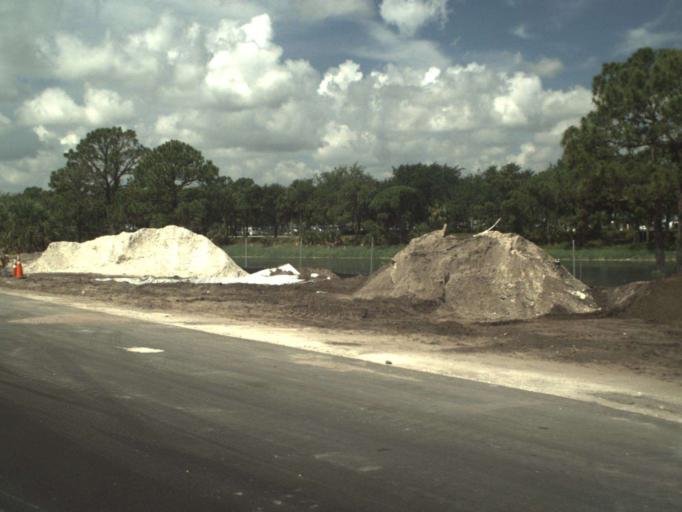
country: US
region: Florida
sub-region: Broward County
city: Deerfield Beach
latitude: 26.3088
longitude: -80.1186
